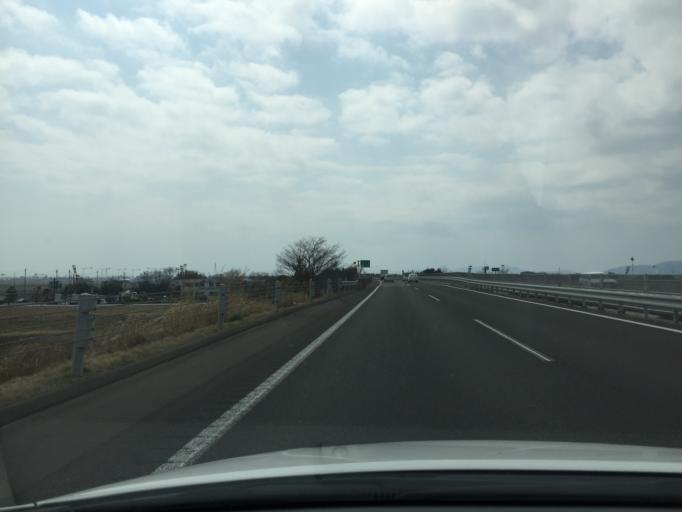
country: JP
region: Miyagi
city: Iwanuma
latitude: 38.1397
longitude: 140.8897
